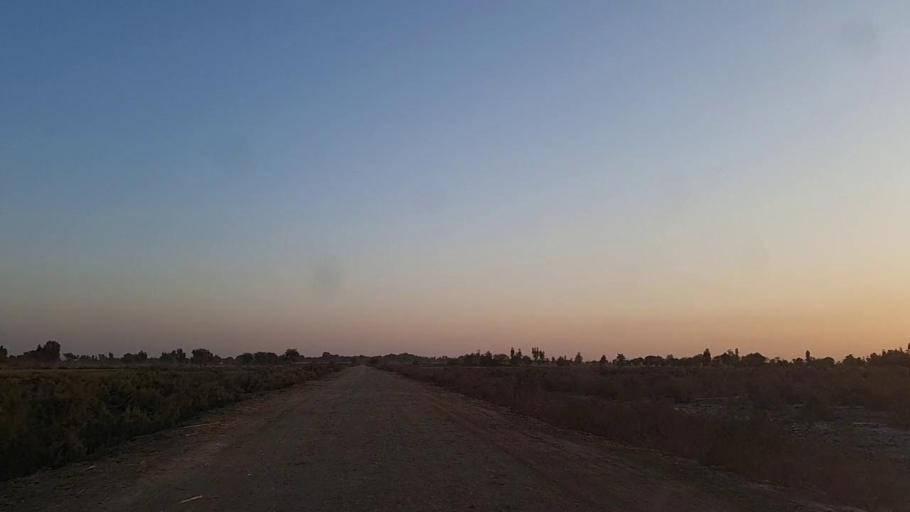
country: PK
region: Sindh
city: Samaro
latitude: 25.3162
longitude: 69.3693
